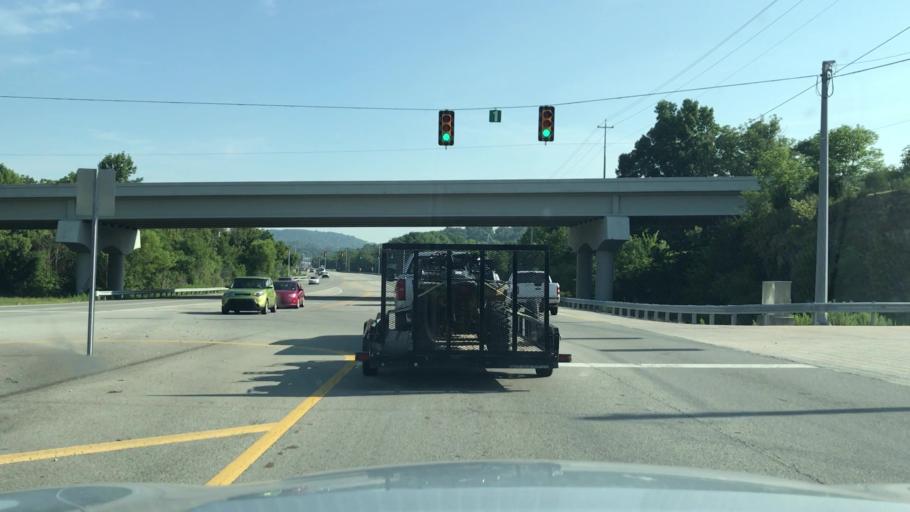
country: US
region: Tennessee
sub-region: Overton County
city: Livingston
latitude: 36.3601
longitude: -85.3415
